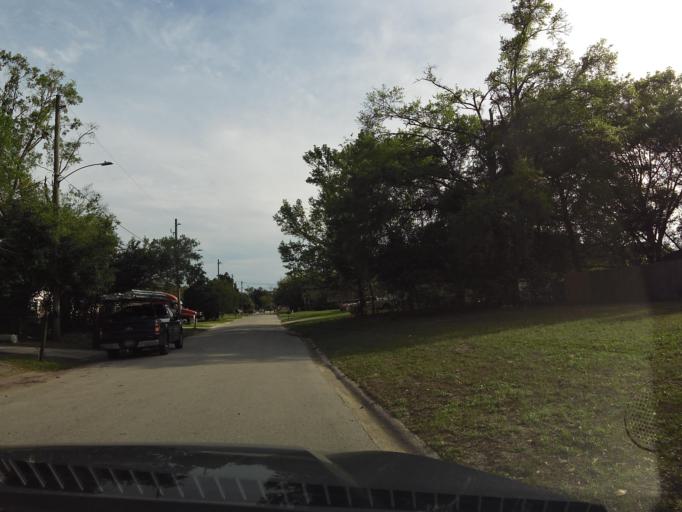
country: US
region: Florida
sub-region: Clay County
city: Bellair-Meadowbrook Terrace
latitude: 30.2429
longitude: -81.7694
